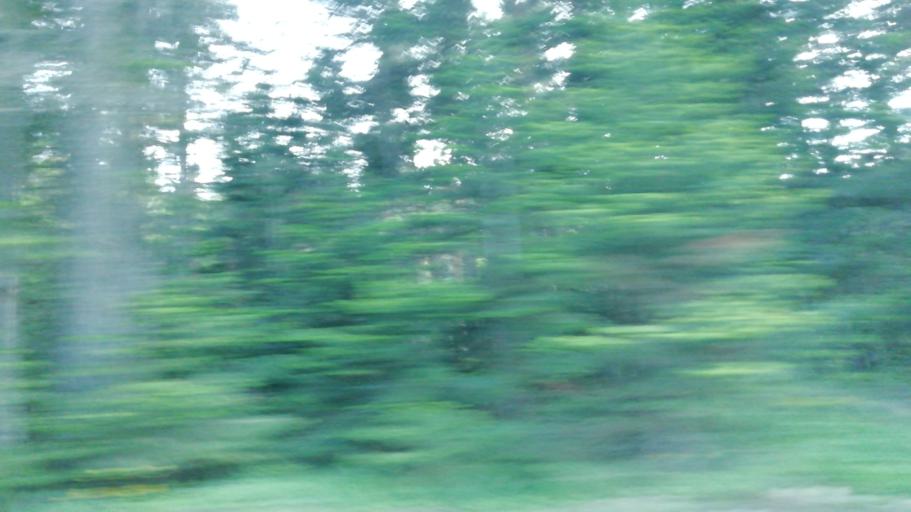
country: TR
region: Karabuk
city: Eskipazar
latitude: 41.0480
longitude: 32.5449
